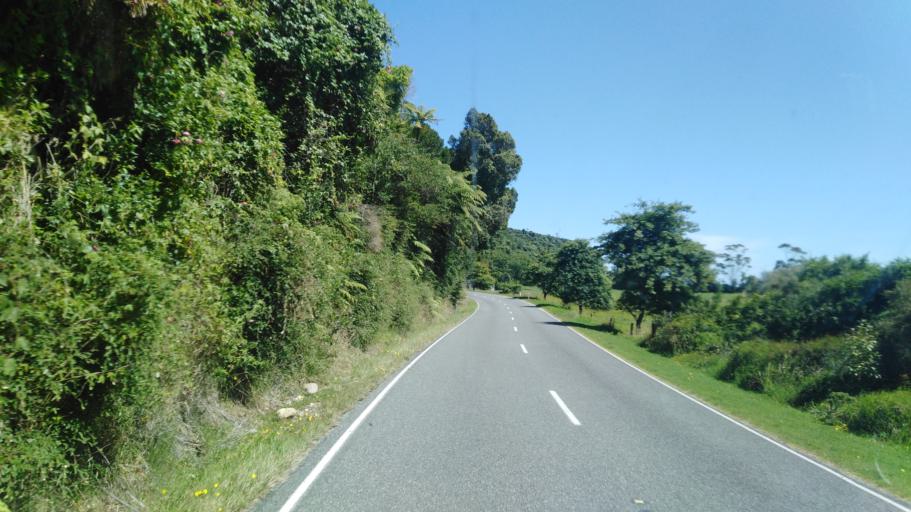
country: NZ
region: West Coast
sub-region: Buller District
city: Westport
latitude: -41.2605
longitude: 172.1249
